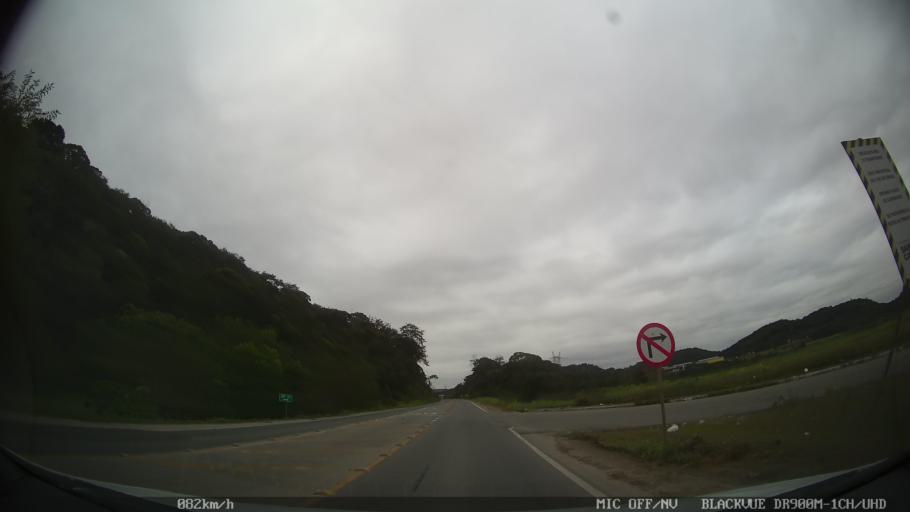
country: BR
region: Santa Catarina
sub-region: Joinville
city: Joinville
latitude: -26.2604
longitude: -48.9117
